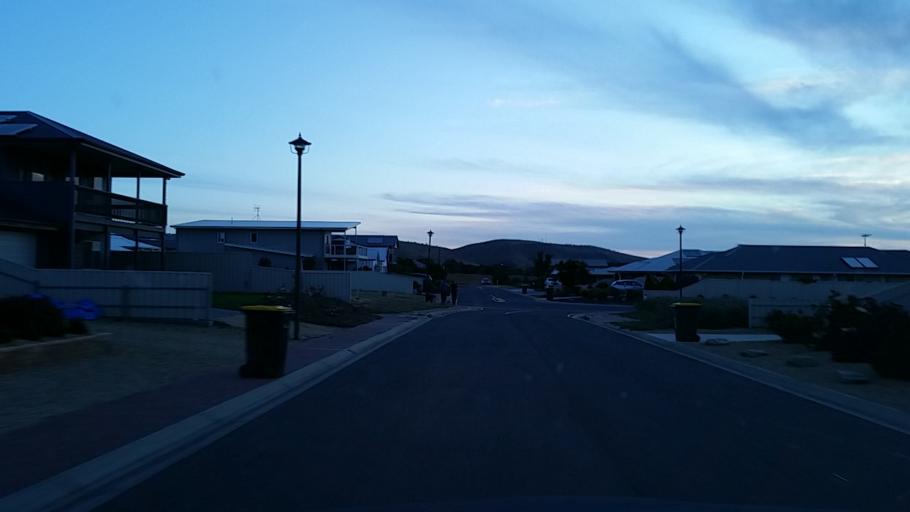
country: AU
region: South Australia
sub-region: Yankalilla
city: Normanville
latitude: -35.4521
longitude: 138.3159
